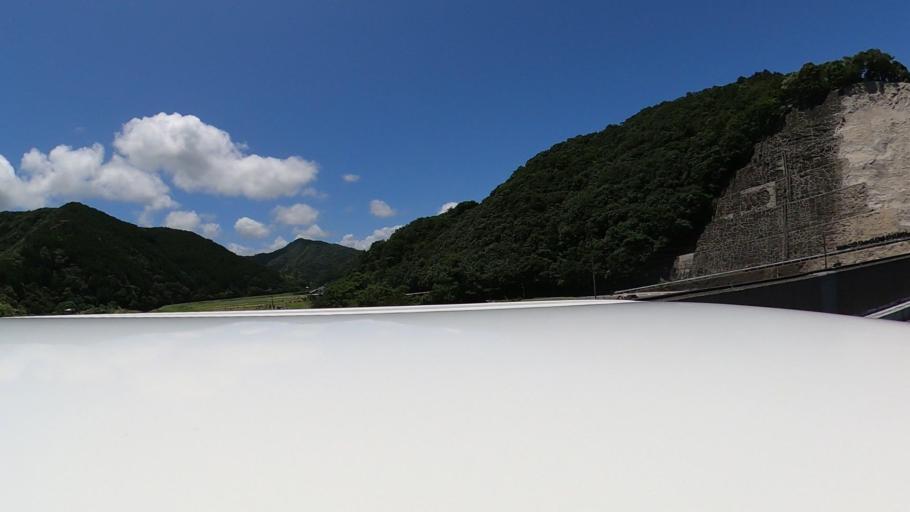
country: JP
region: Miyazaki
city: Nobeoka
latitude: 32.5236
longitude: 131.6651
